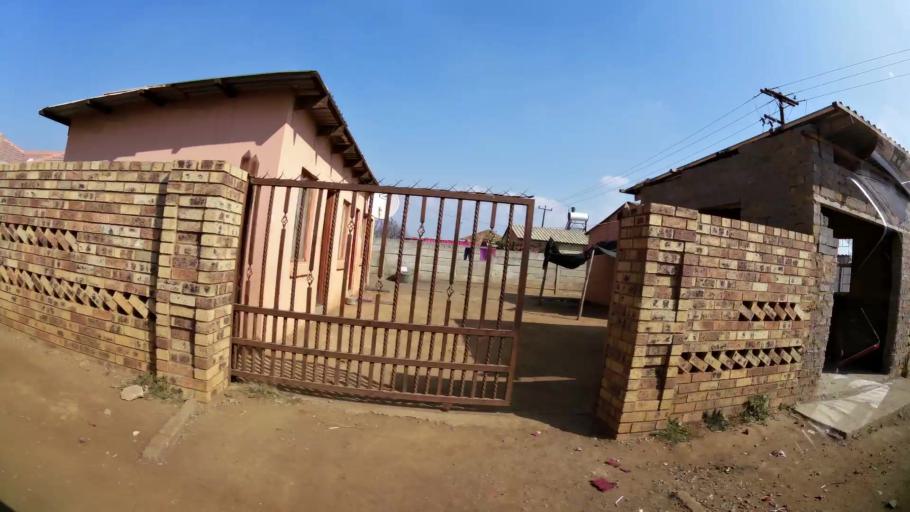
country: ZA
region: Gauteng
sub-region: Ekurhuleni Metropolitan Municipality
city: Springs
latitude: -26.1094
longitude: 28.4825
